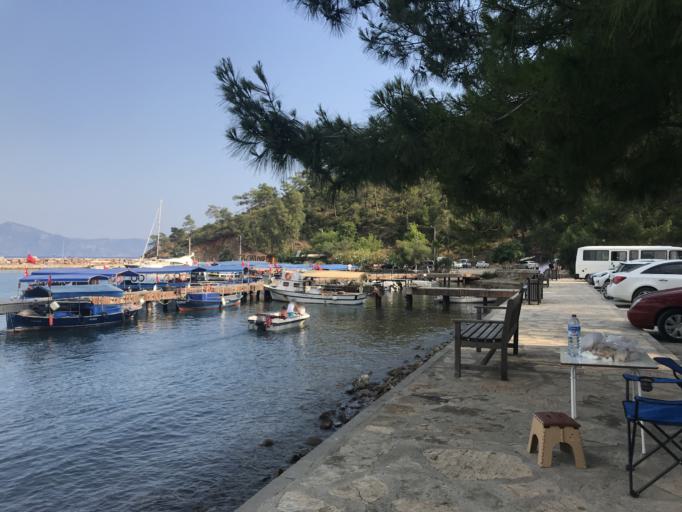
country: TR
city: Dalyan
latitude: 36.8291
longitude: 28.5483
